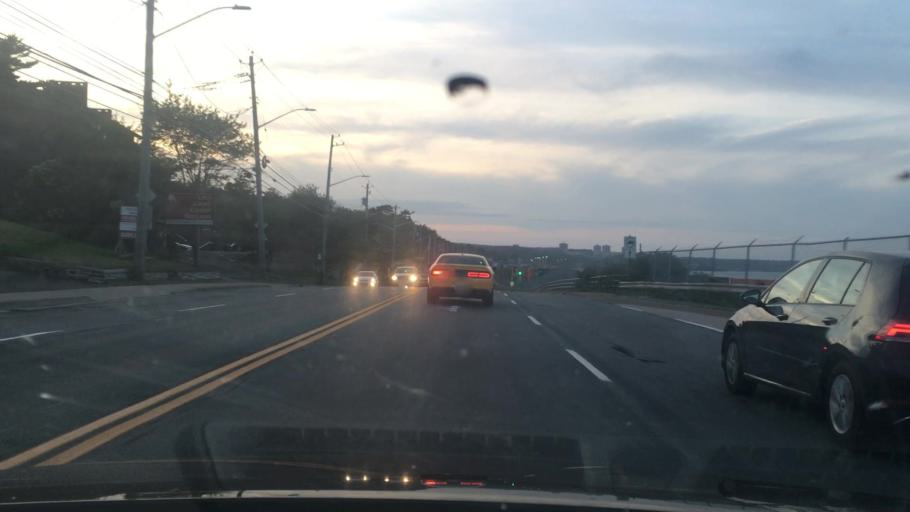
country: CA
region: Nova Scotia
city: Dartmouth
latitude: 44.6653
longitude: -63.6355
